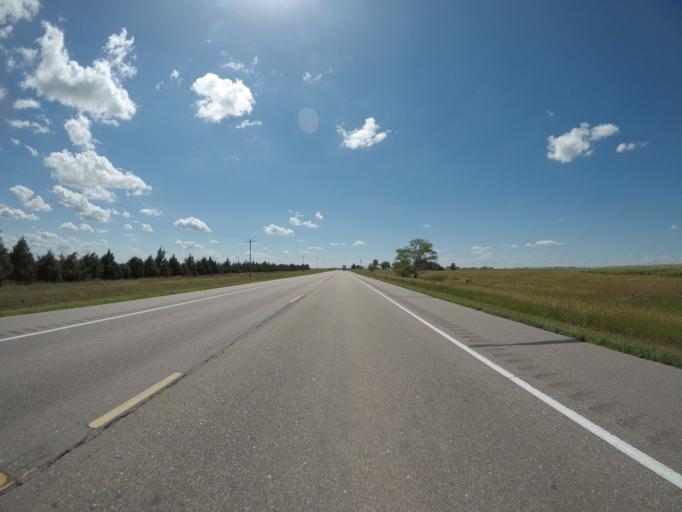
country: US
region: Nebraska
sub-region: Chase County
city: Imperial
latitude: 40.4945
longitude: -101.5780
